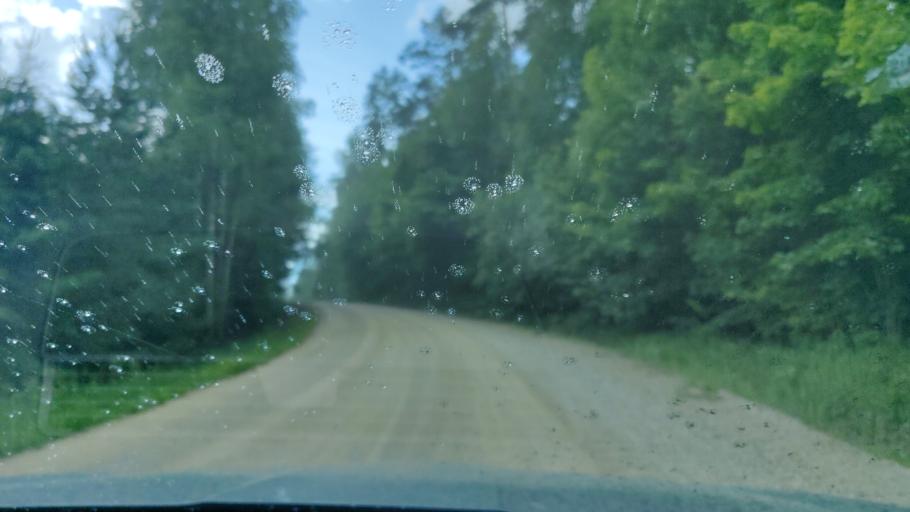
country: EE
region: Vorumaa
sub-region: Antsla vald
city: Vana-Antsla
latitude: 58.0205
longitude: 26.5784
